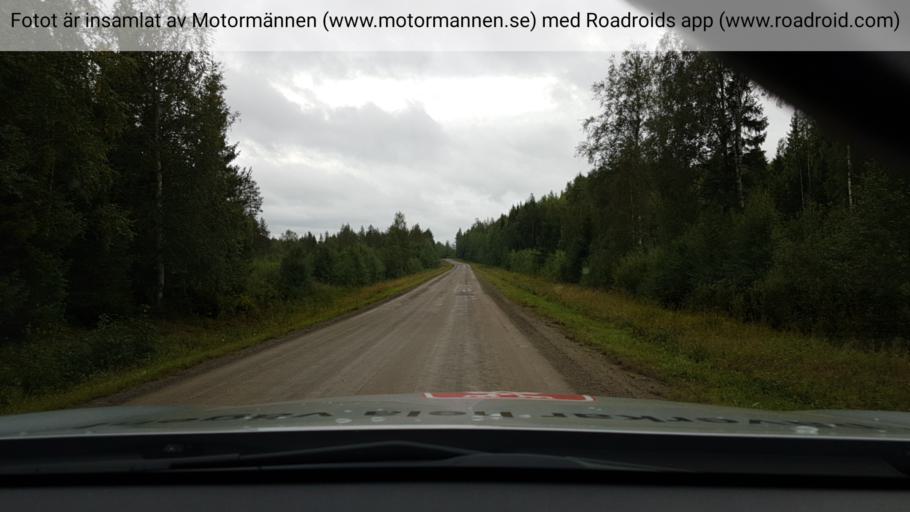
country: SE
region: Vaesterbotten
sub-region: Skelleftea Kommun
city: Burtraesk
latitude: 64.3217
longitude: 20.6377
